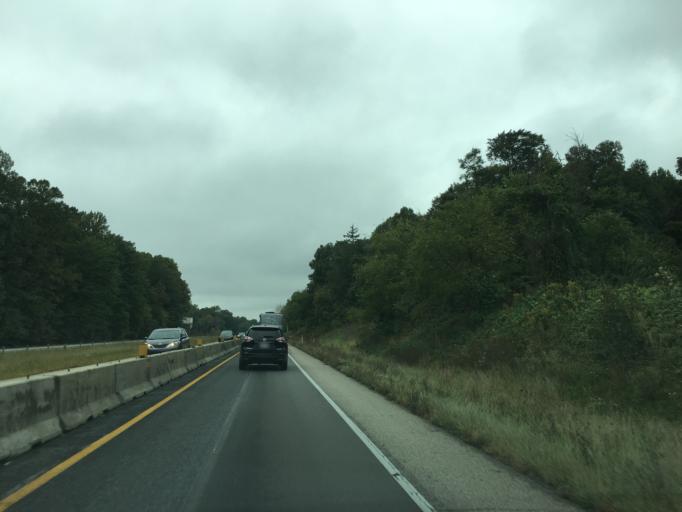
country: US
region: Indiana
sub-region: Ripley County
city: Sunman
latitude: 39.2805
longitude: -85.1217
